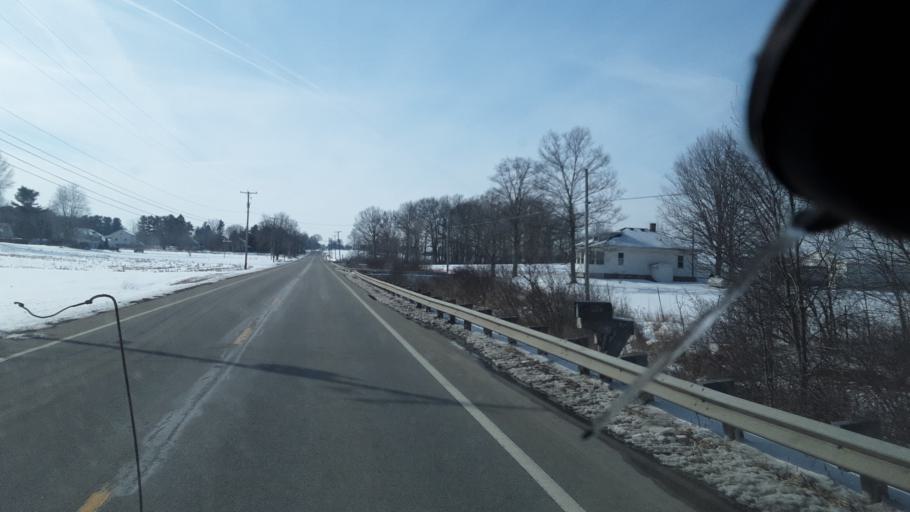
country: US
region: Ohio
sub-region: Mahoning County
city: Canfield
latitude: 41.0242
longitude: -80.8839
